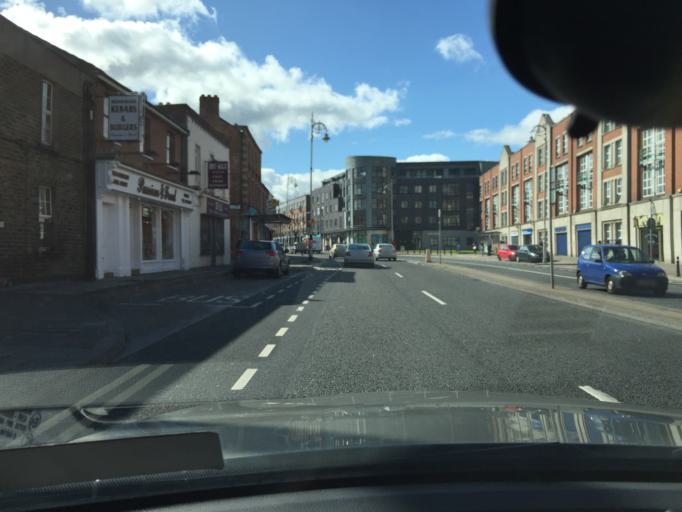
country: IE
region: Leinster
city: Rathmines
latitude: 53.3347
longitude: -6.2742
